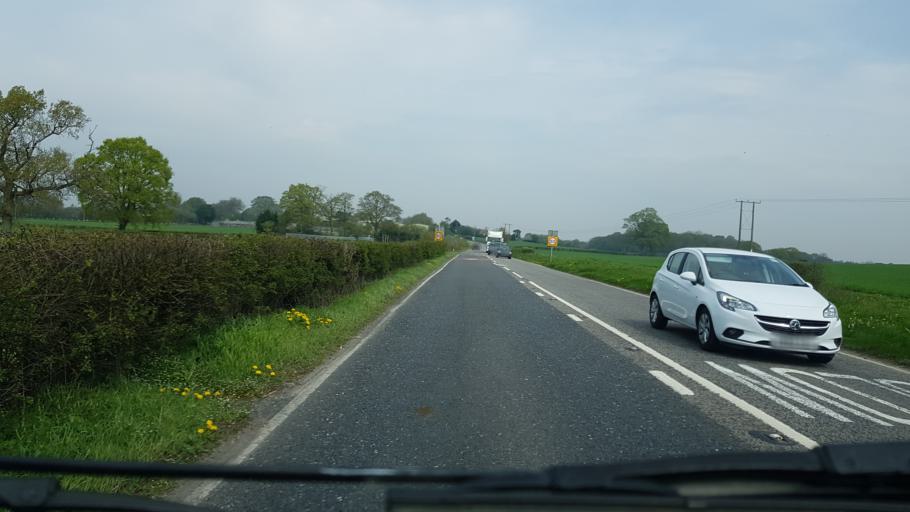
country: GB
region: England
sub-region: Hampshire
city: Kingsclere
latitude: 51.3360
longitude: -1.2591
